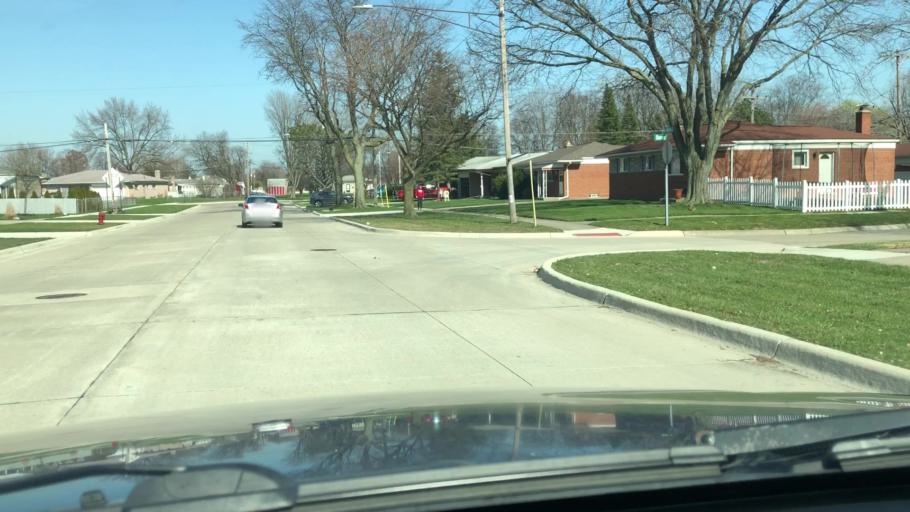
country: US
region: Michigan
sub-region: Macomb County
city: Center Line
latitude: 42.5002
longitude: -82.9930
